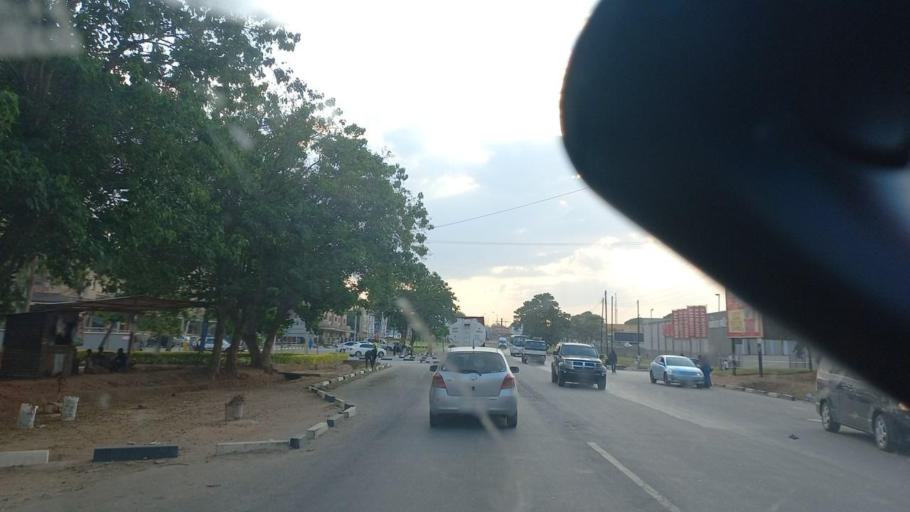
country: ZM
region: Lusaka
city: Lusaka
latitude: -15.3703
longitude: 28.4035
